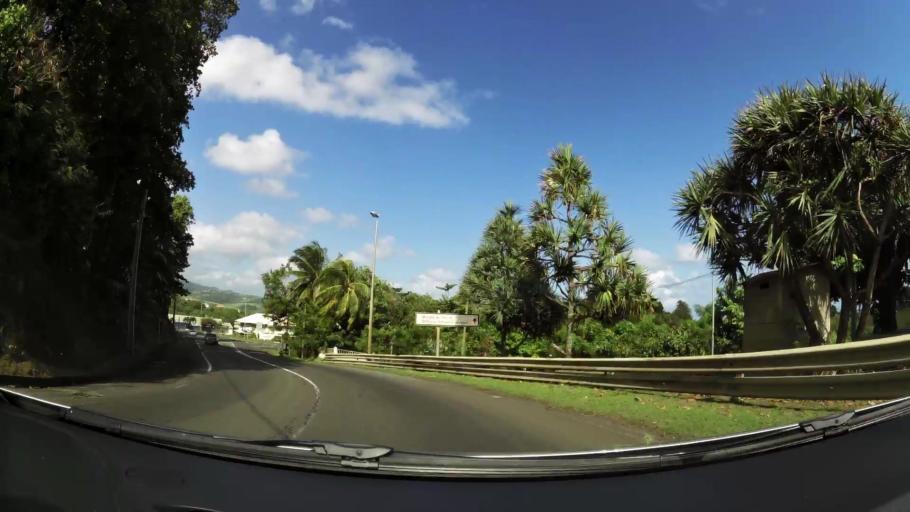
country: MQ
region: Martinique
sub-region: Martinique
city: Sainte-Marie
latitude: 14.7745
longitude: -60.9851
